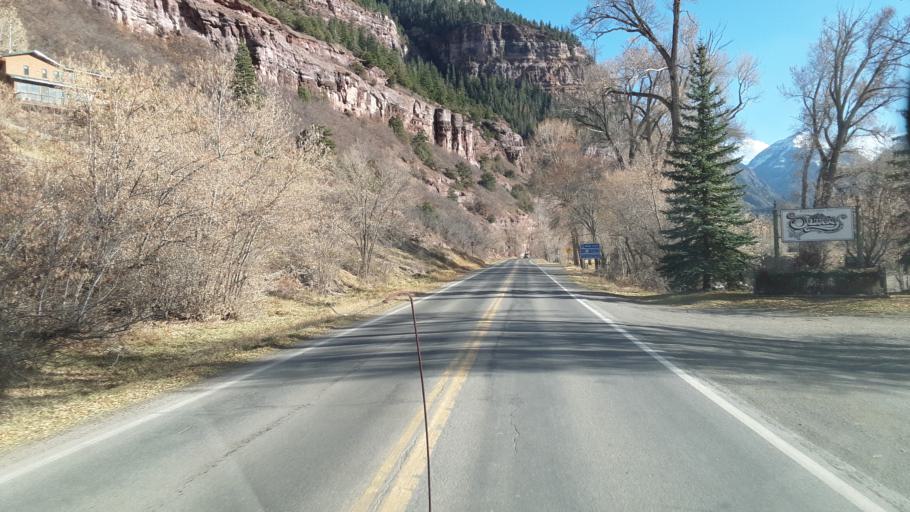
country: US
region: Colorado
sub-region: Ouray County
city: Ouray
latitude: 38.0512
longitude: -107.6852
